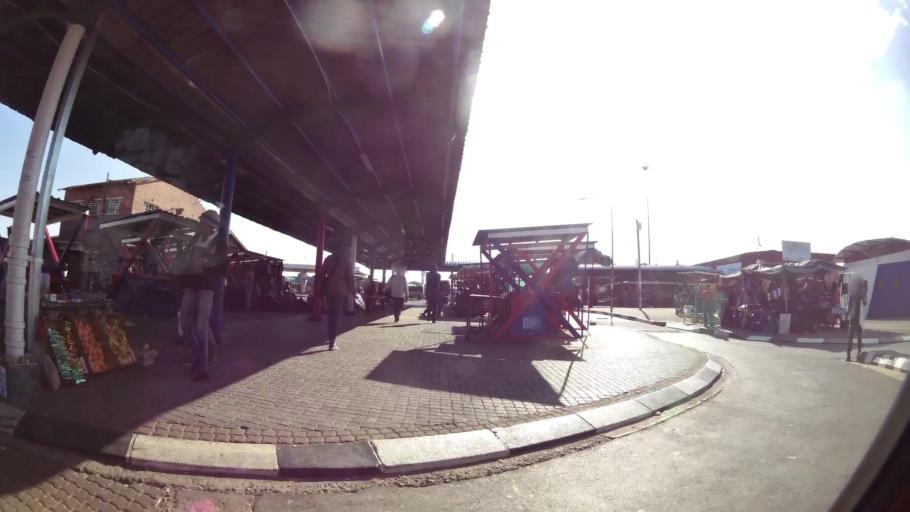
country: ZA
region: Gauteng
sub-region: City of Johannesburg Metropolitan Municipality
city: Soweto
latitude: -26.2304
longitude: 27.8765
